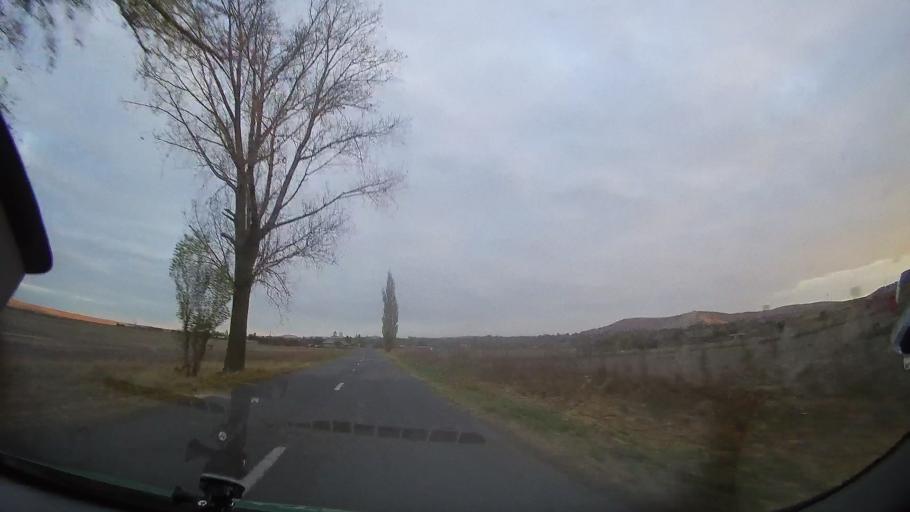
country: RO
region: Tulcea
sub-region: Comuna Mihai Bravu
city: Turda
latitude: 44.9839
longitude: 28.6130
